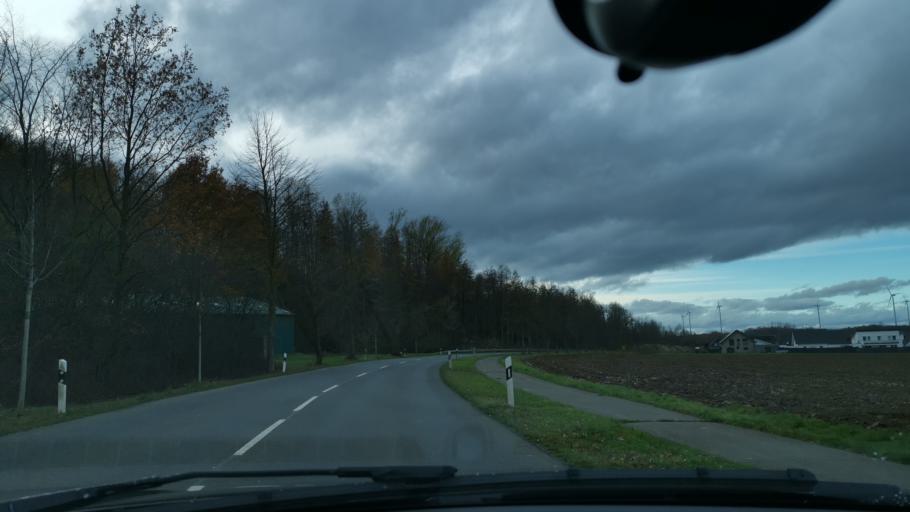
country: DE
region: North Rhine-Westphalia
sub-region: Regierungsbezirk Koln
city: Bedburg
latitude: 51.0406
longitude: 6.5833
